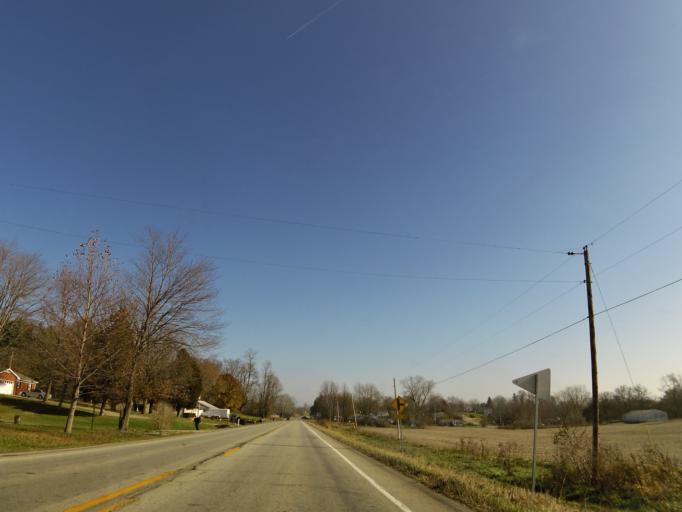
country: US
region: Indiana
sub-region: Fayette County
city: Connersville
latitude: 39.6342
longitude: -85.2080
